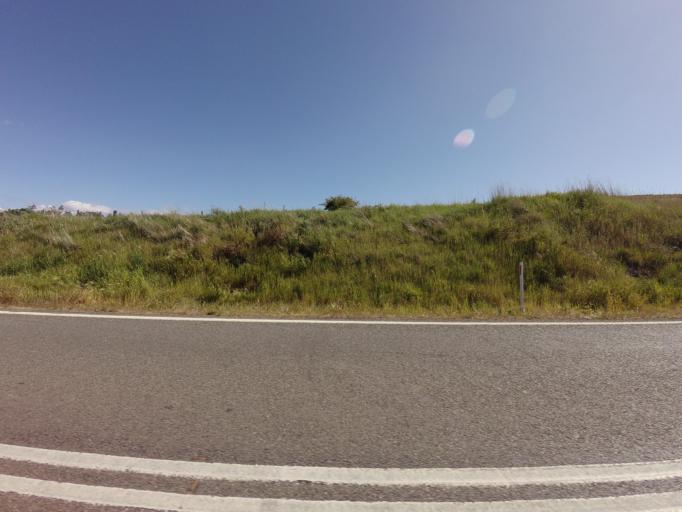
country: AU
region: Tasmania
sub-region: Derwent Valley
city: New Norfolk
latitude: -42.6426
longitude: 146.9197
